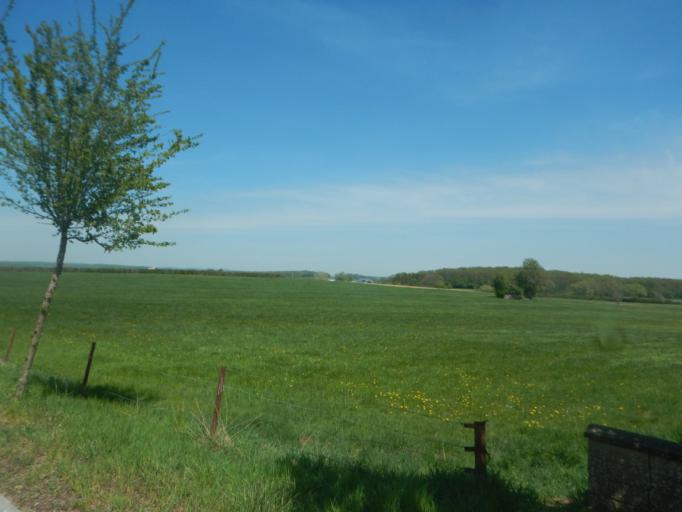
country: LU
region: Diekirch
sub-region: Canton de Redange
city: Beckerich
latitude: 49.7448
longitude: 5.9188
